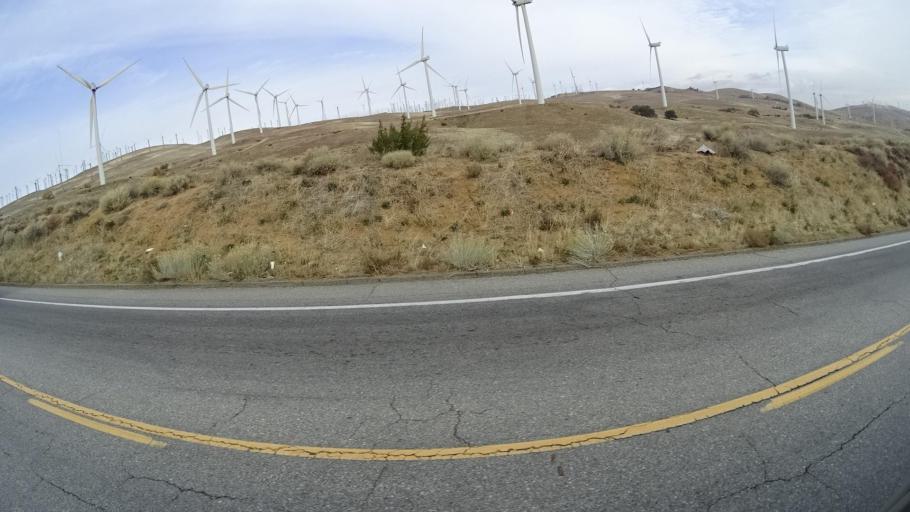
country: US
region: California
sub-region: Kern County
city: Tehachapi
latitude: 35.0557
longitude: -118.3775
